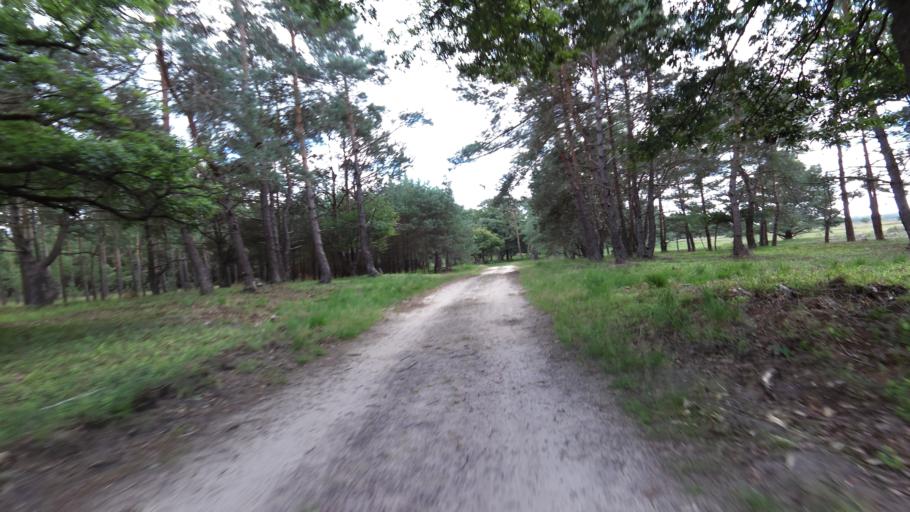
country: NL
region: Gelderland
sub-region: Gemeente Apeldoorn
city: Uddel
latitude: 52.2396
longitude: 5.8079
